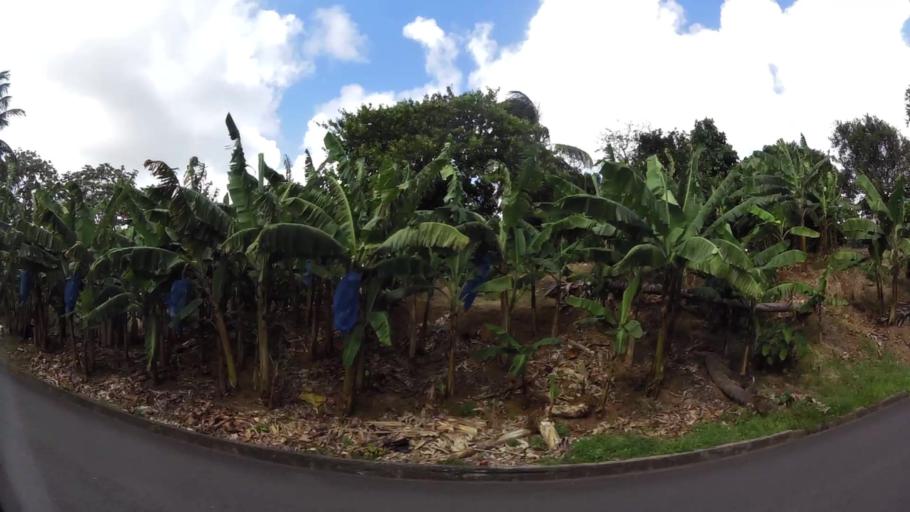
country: LC
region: Dennery Quarter
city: Dennery
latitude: 13.9336
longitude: -60.9246
